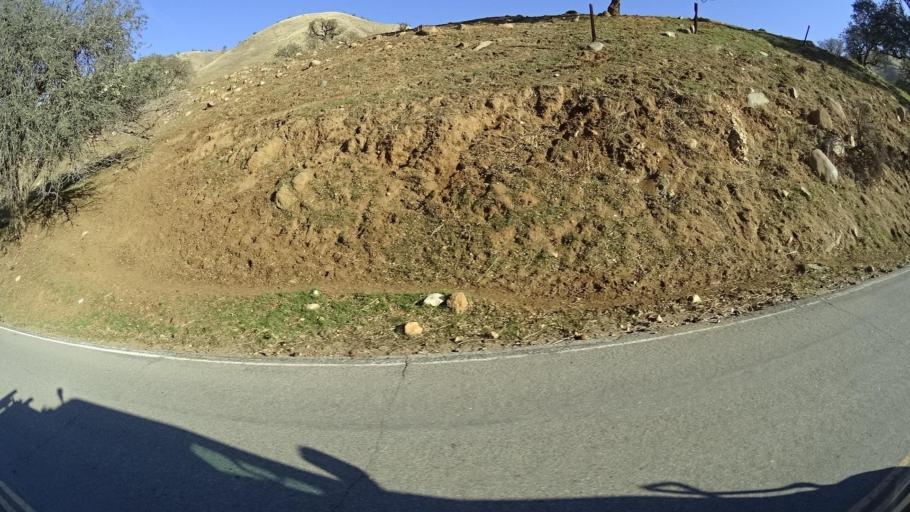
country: US
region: California
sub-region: Kern County
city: Bear Valley Springs
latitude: 35.2993
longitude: -118.5925
